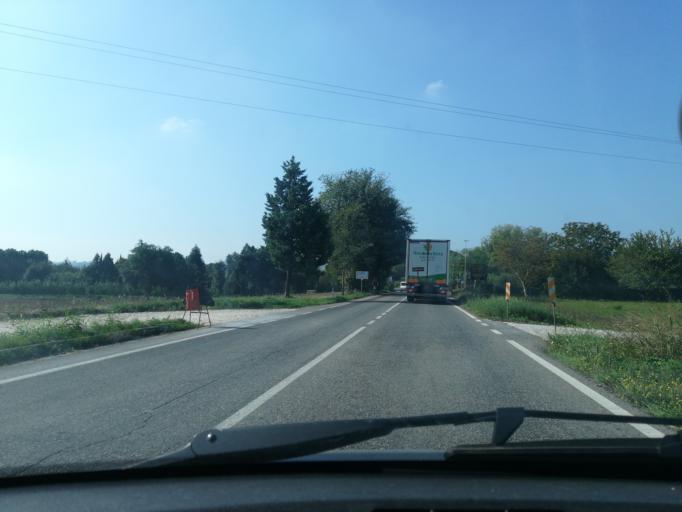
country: IT
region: The Marches
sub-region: Provincia di Macerata
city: Piediripa
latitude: 43.2713
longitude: 13.4718
